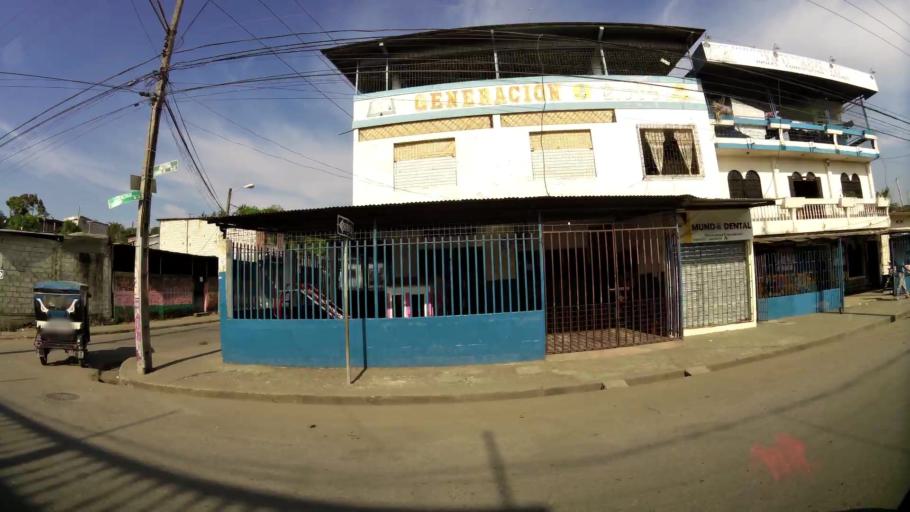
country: EC
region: Guayas
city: Eloy Alfaro
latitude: -2.0722
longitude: -79.9284
